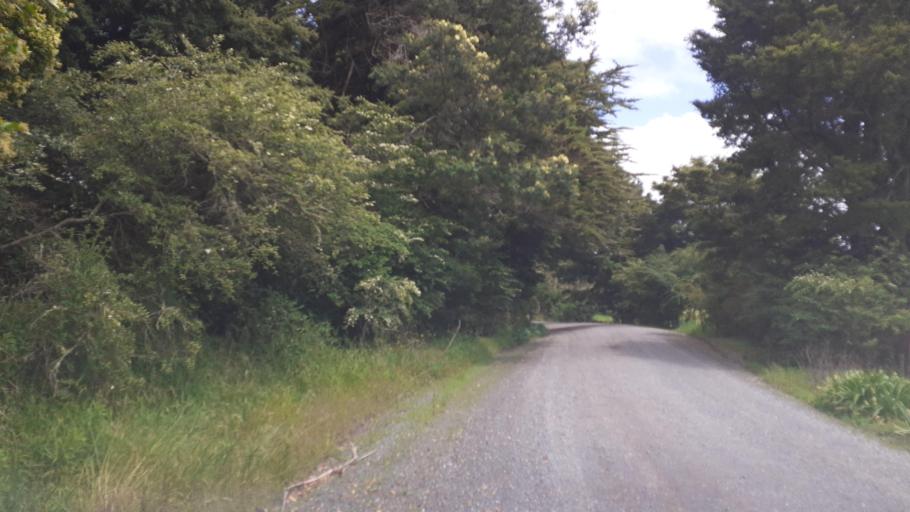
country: NZ
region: Northland
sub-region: Far North District
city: Kawakawa
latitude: -35.5162
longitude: 174.0809
